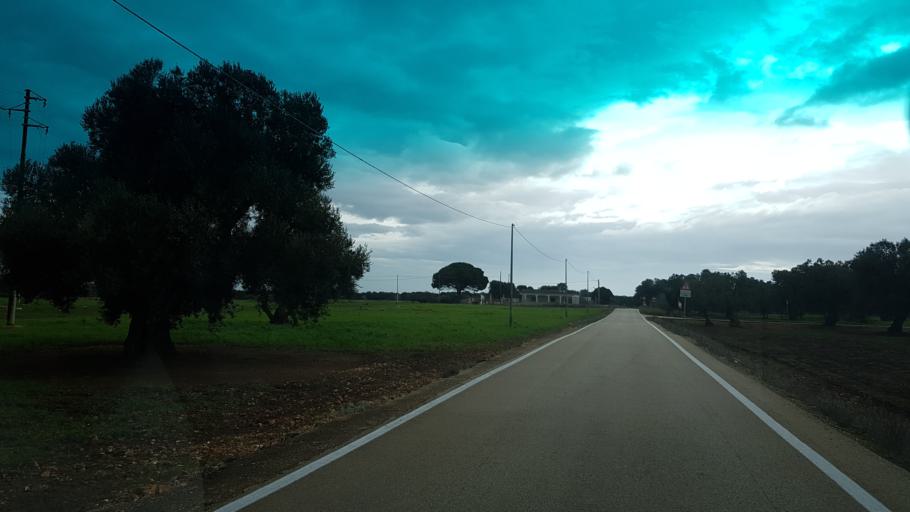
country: IT
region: Apulia
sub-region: Provincia di Brindisi
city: San Vito dei Normanni
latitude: 40.7114
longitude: 17.7660
